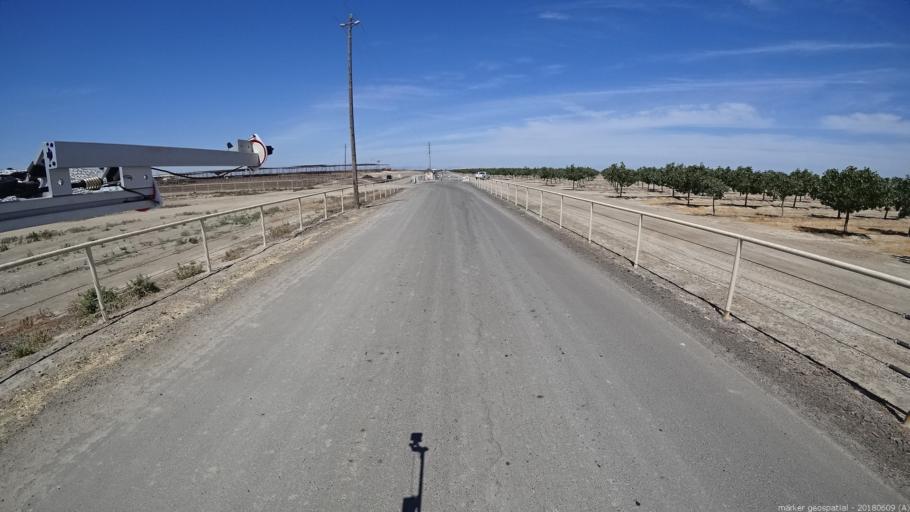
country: US
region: California
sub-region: Fresno County
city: Firebaugh
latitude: 36.9524
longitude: -120.4140
